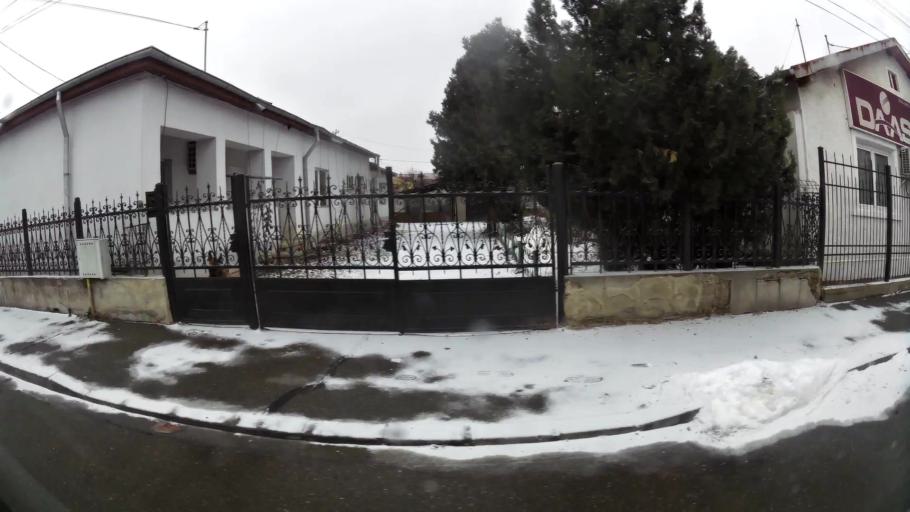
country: RO
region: Prahova
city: Ploiesti
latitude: 44.9494
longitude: 26.0157
